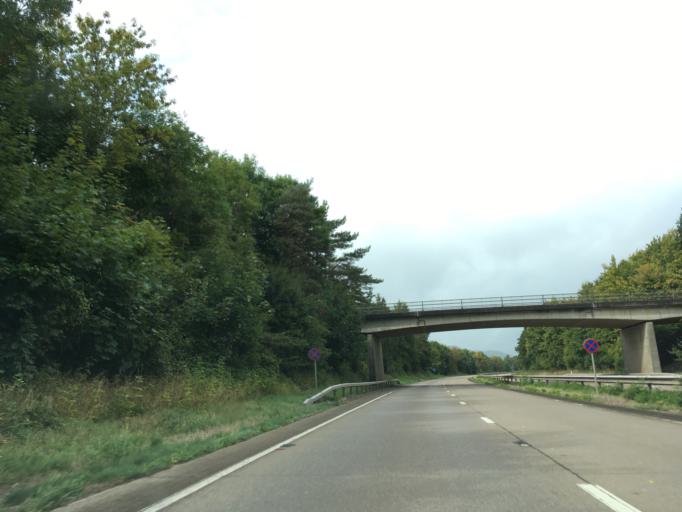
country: GB
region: Wales
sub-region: Monmouthshire
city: Abergavenny
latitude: 51.7857
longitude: -2.9815
